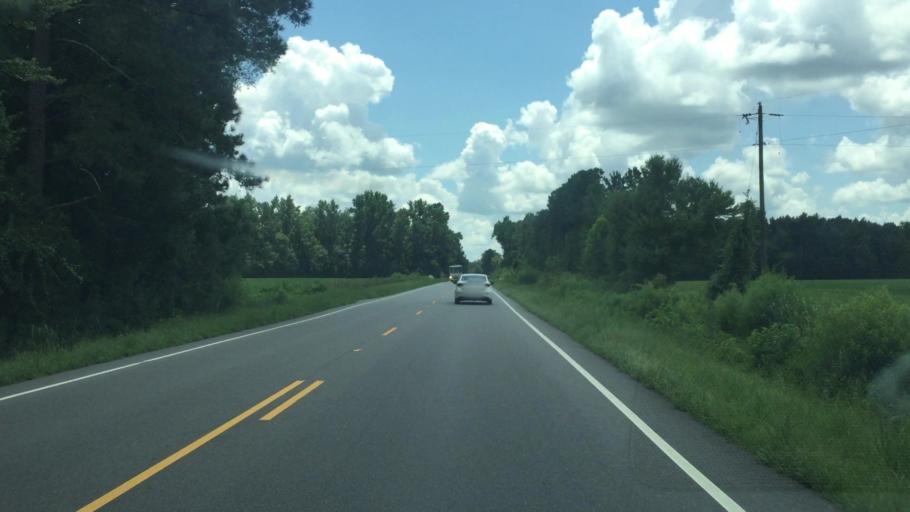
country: US
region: North Carolina
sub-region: Columbus County
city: Tabor City
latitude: 34.1941
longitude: -78.8359
